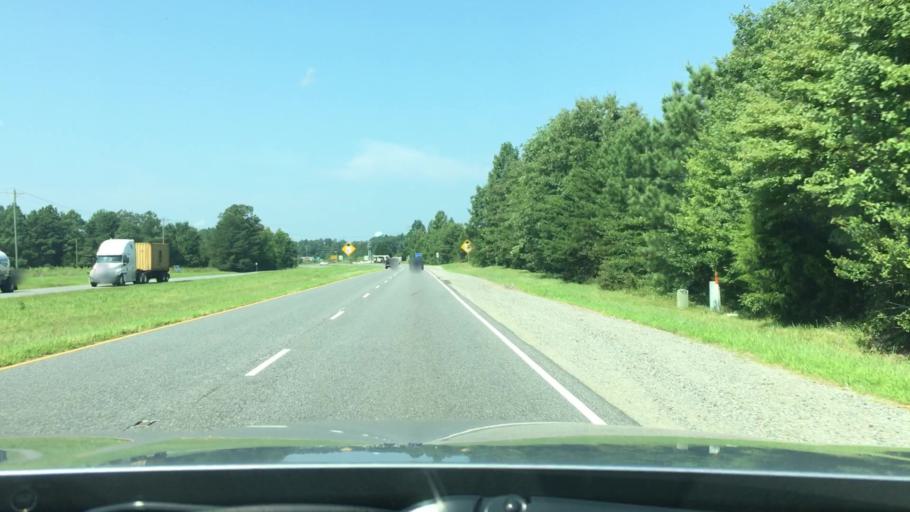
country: US
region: Virginia
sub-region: Caroline County
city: Bowling Green
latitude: 37.9443
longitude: -77.4529
